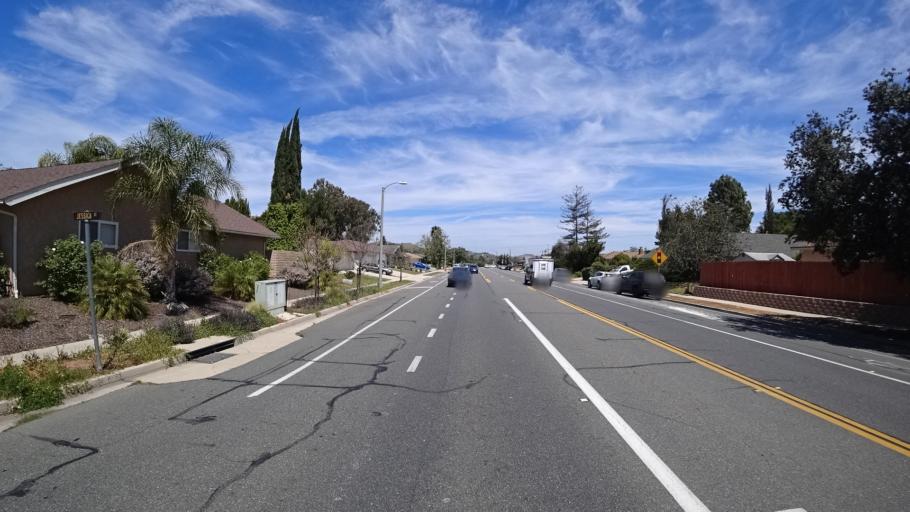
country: US
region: California
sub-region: Ventura County
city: Casa Conejo
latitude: 34.1777
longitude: -118.9450
